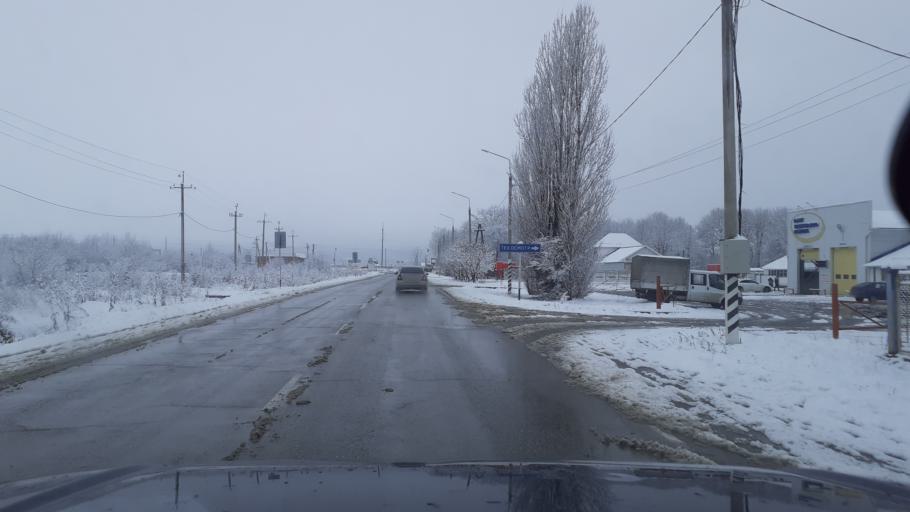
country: RU
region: Adygeya
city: Tul'skiy
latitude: 44.4955
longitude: 40.1681
